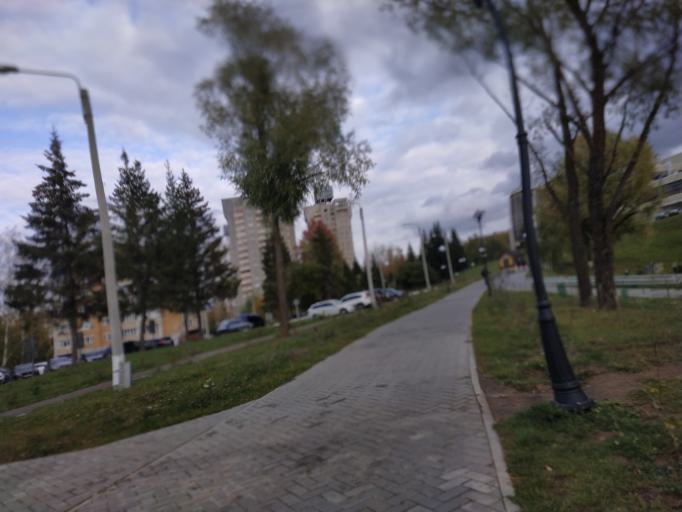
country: RU
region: Chuvashia
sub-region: Cheboksarskiy Rayon
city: Cheboksary
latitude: 56.1469
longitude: 47.2132
